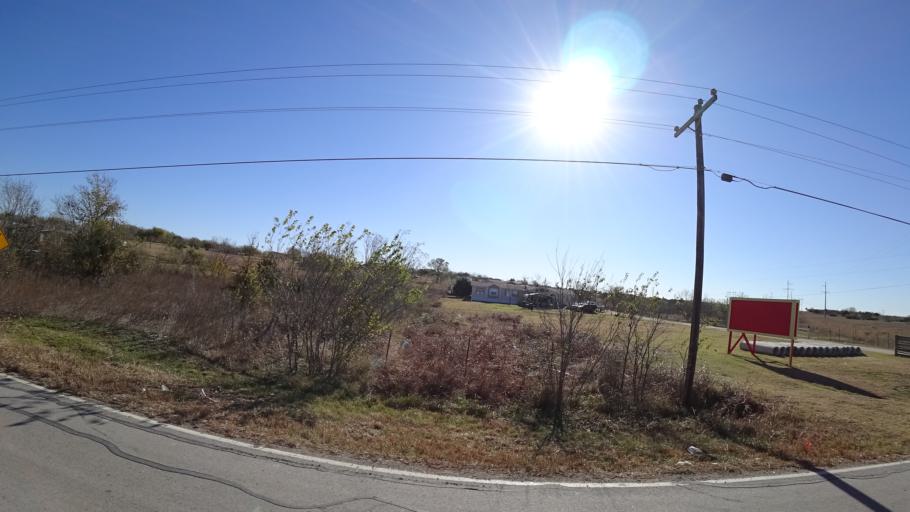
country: US
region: Texas
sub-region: Travis County
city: Onion Creek
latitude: 30.1057
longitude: -97.6758
